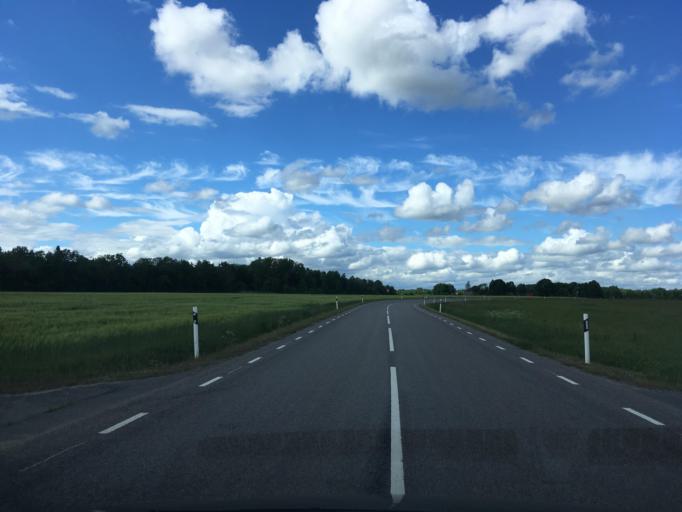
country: EE
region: Paernumaa
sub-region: Halinga vald
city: Parnu-Jaagupi
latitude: 58.6316
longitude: 24.5453
